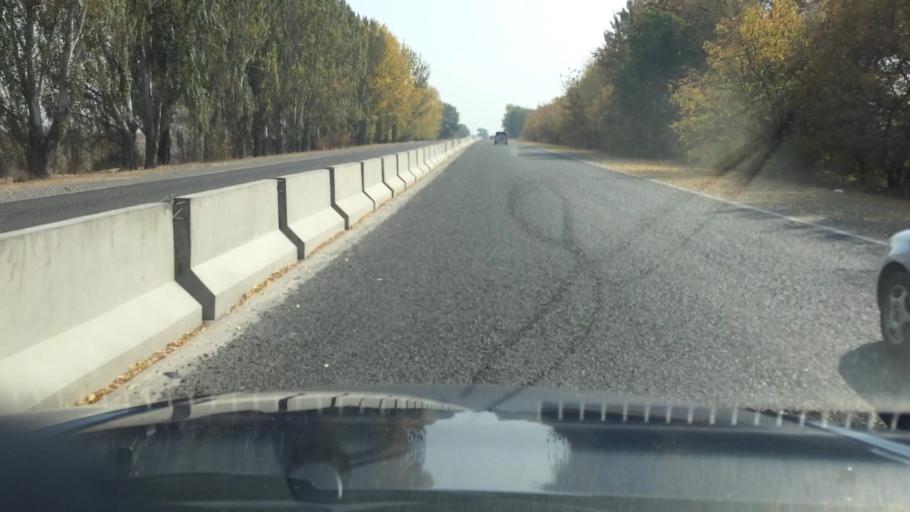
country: KG
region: Chuy
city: Kant
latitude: 42.9640
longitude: 74.9151
